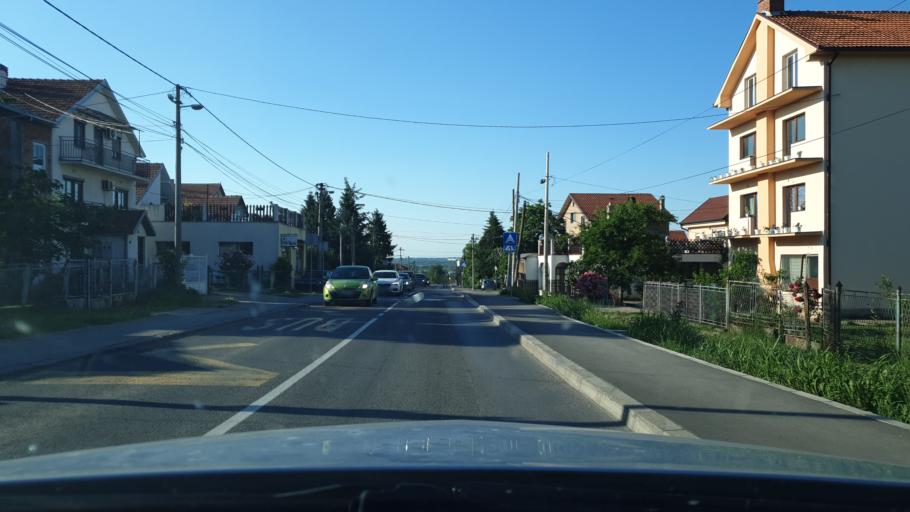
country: RS
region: Central Serbia
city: Sremcica
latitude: 44.7166
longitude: 20.3683
